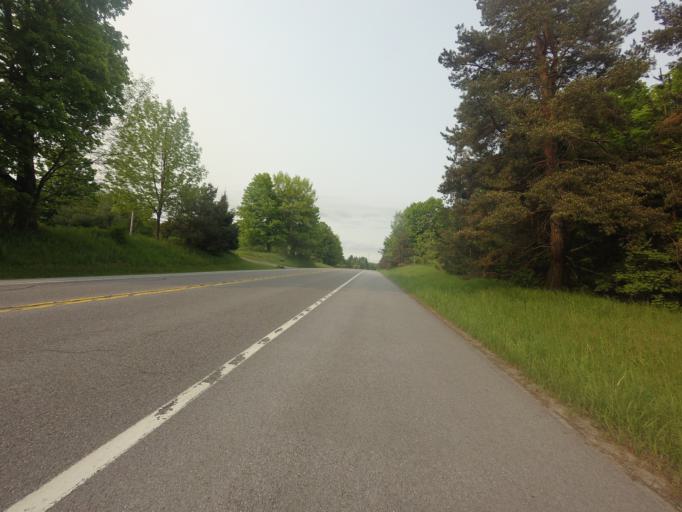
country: US
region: New York
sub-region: Jefferson County
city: Carthage
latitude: 44.0462
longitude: -75.5629
